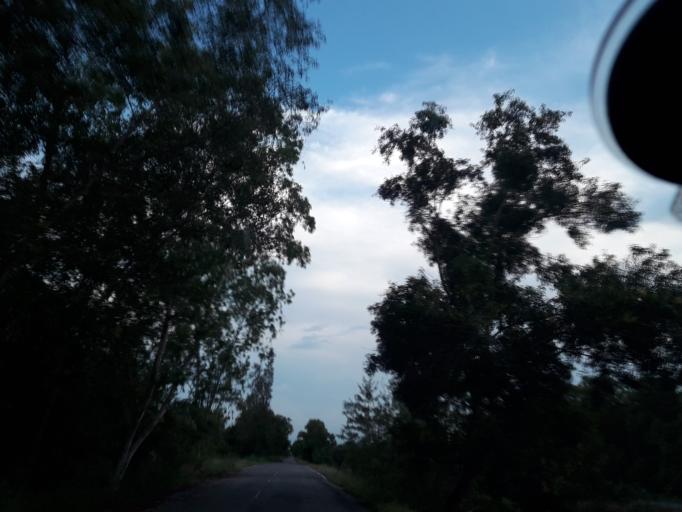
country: TH
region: Pathum Thani
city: Nong Suea
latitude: 14.2272
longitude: 100.8688
